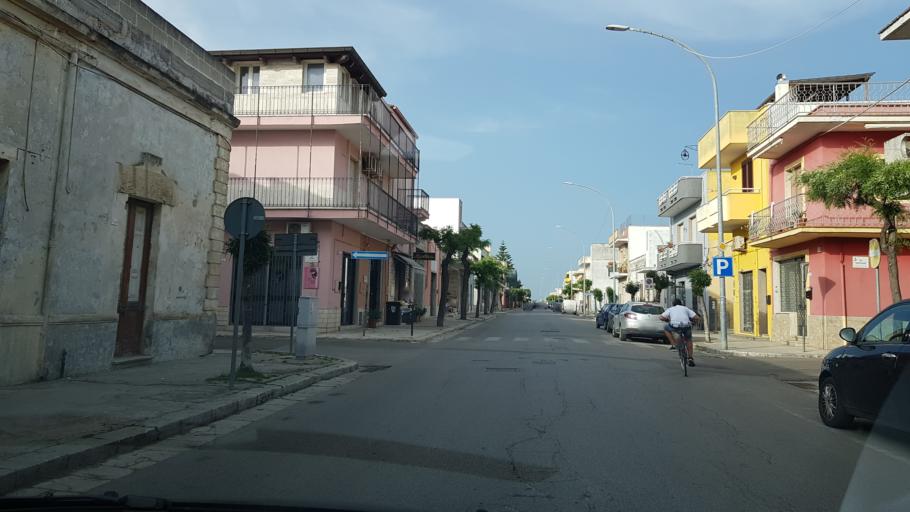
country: IT
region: Apulia
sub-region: Provincia di Brindisi
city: San Donaci
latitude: 40.4499
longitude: 17.9269
